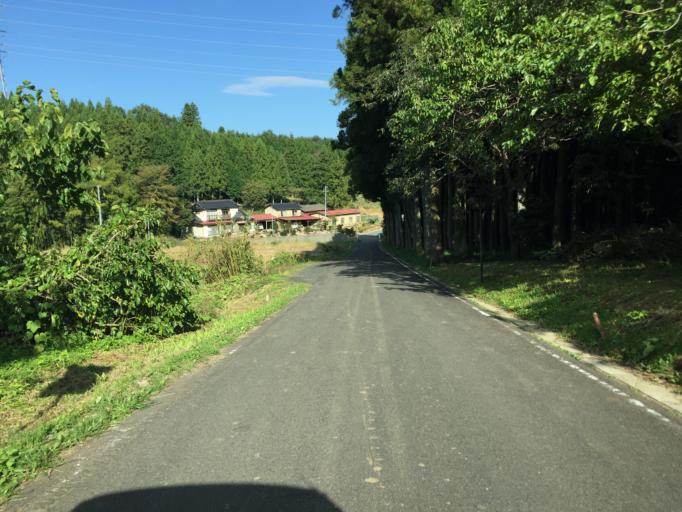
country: JP
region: Fukushima
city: Fukushima-shi
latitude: 37.6717
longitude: 140.4276
